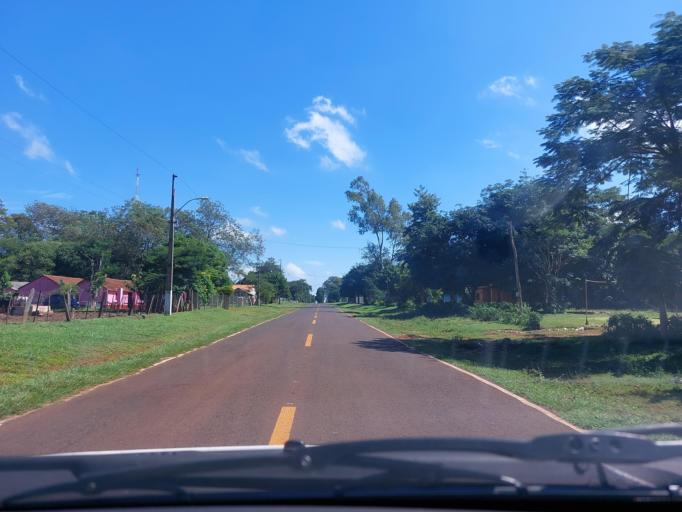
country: PY
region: San Pedro
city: Guayaybi
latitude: -24.5315
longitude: -56.5476
